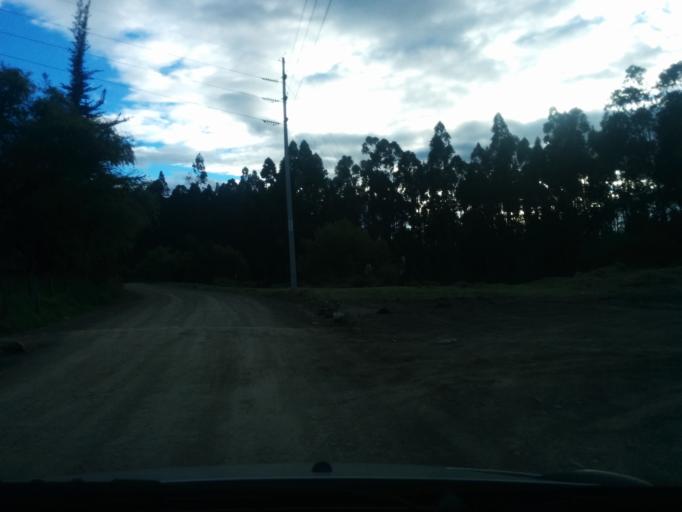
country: EC
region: Azuay
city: Cuenca
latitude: -2.8816
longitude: -78.9473
